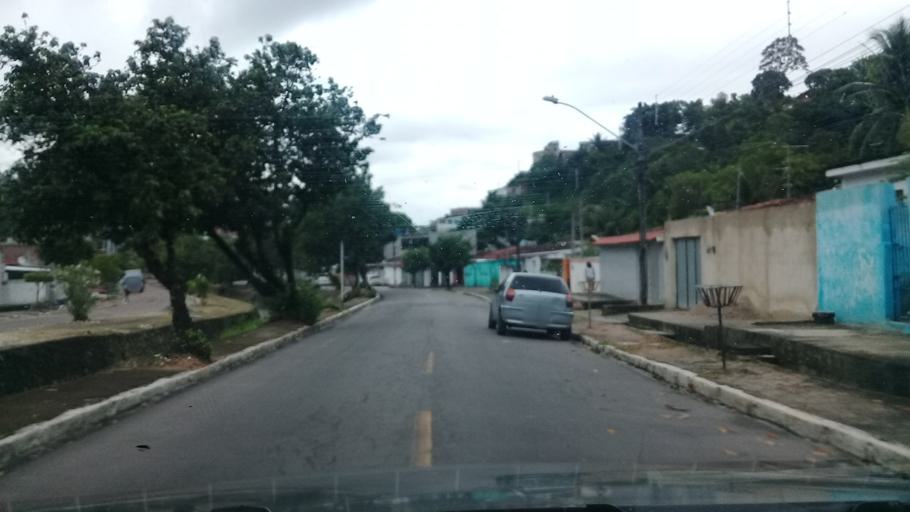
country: BR
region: Pernambuco
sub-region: Jaboatao Dos Guararapes
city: Jaboatao dos Guararapes
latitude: -8.1179
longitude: -34.9518
